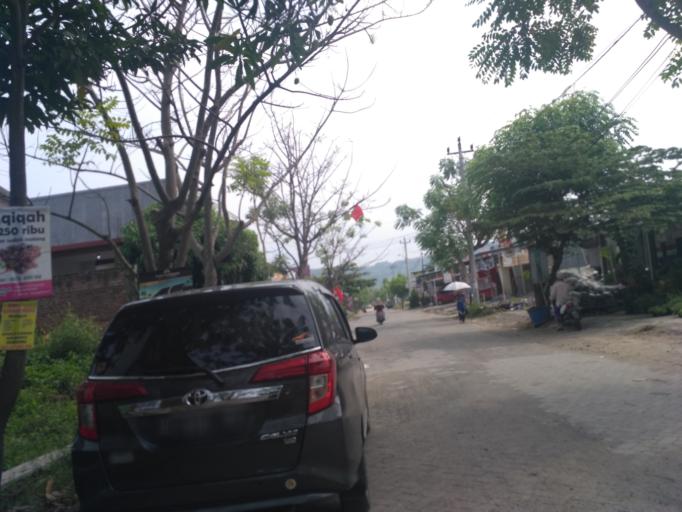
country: ID
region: Central Java
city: Mranggen
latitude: -7.0602
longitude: 110.4697
